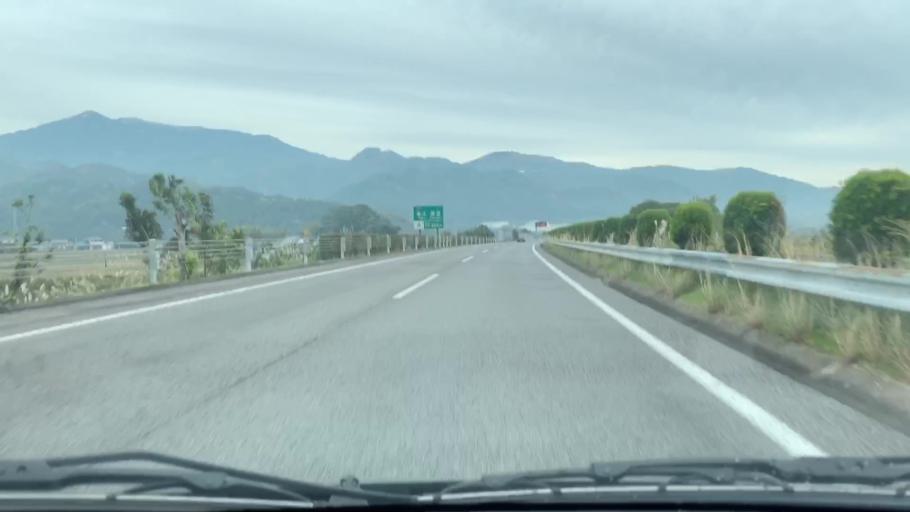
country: JP
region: Saga Prefecture
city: Takeocho-takeo
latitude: 33.2829
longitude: 130.1218
